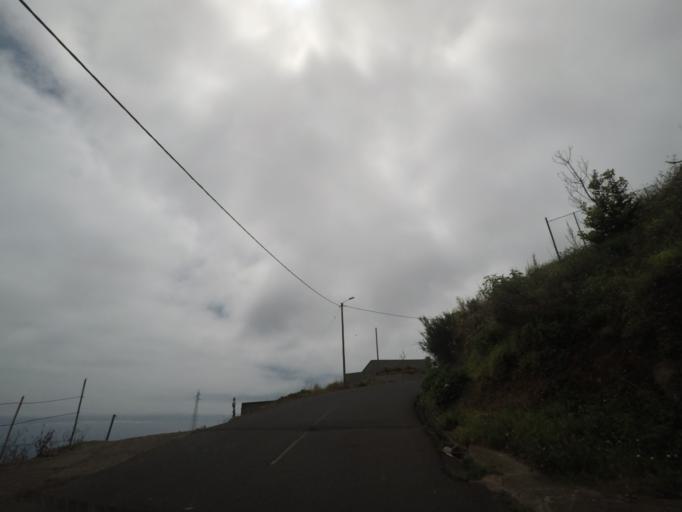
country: PT
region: Madeira
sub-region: Calheta
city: Arco da Calheta
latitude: 32.7080
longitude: -17.1142
